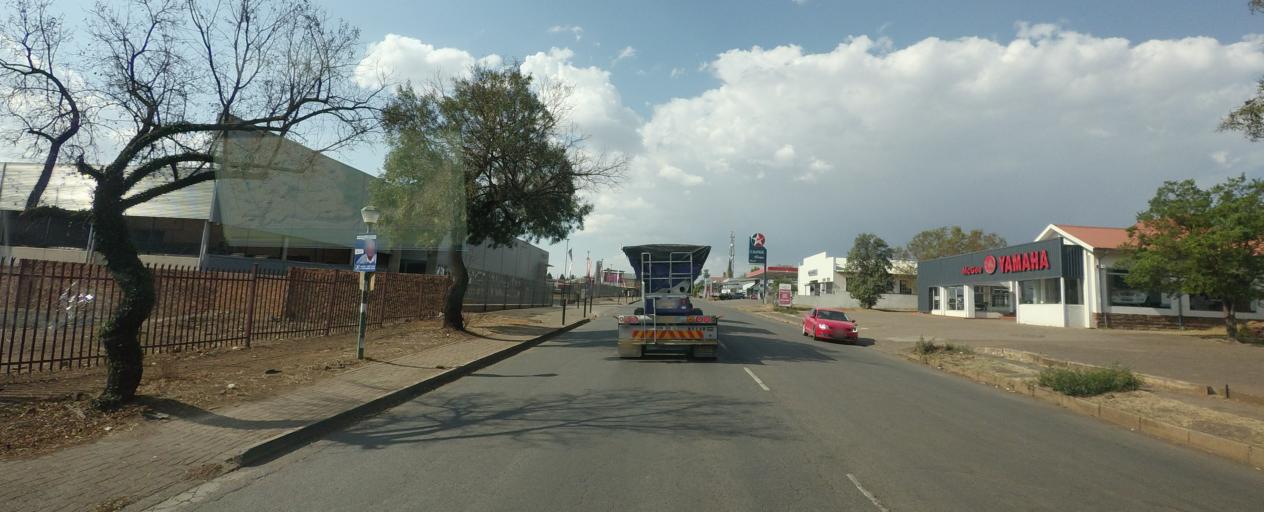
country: ZA
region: Mpumalanga
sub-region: Ehlanzeni District
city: Lydenburg
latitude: -25.0968
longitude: 30.4550
